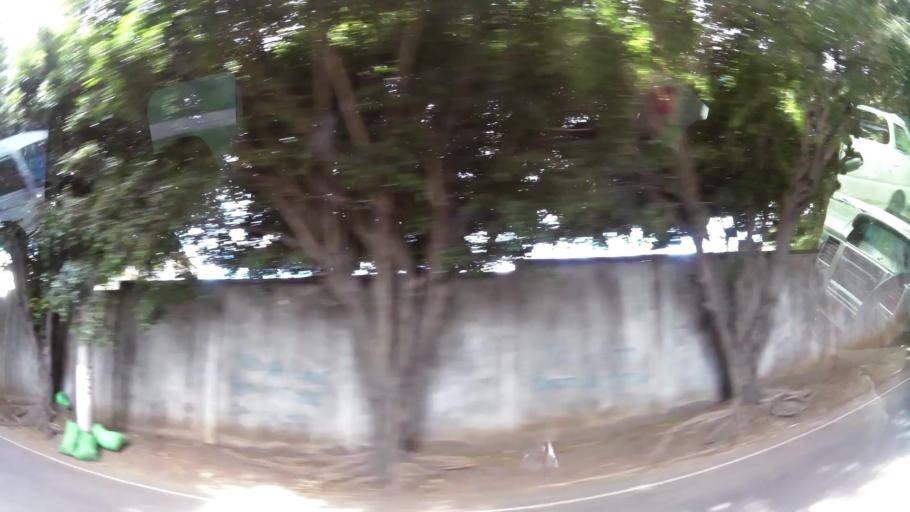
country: GT
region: Guatemala
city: Santa Catarina Pinula
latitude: 14.5835
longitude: -90.5295
